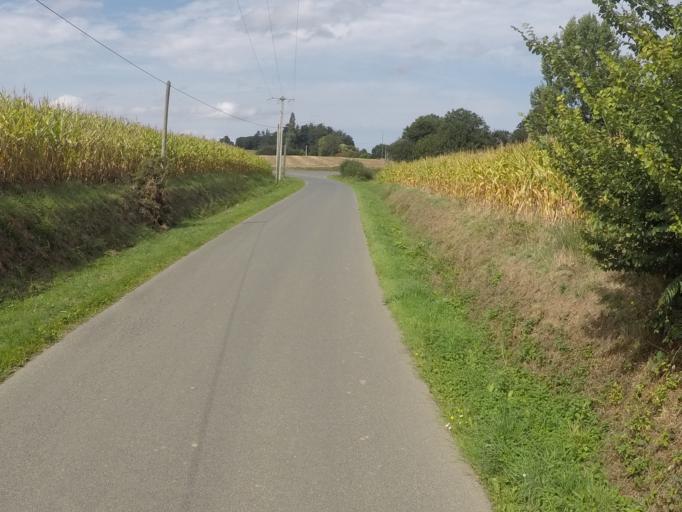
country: FR
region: Brittany
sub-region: Departement des Cotes-d'Armor
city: Goudelin
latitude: 48.6017
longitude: -2.9957
